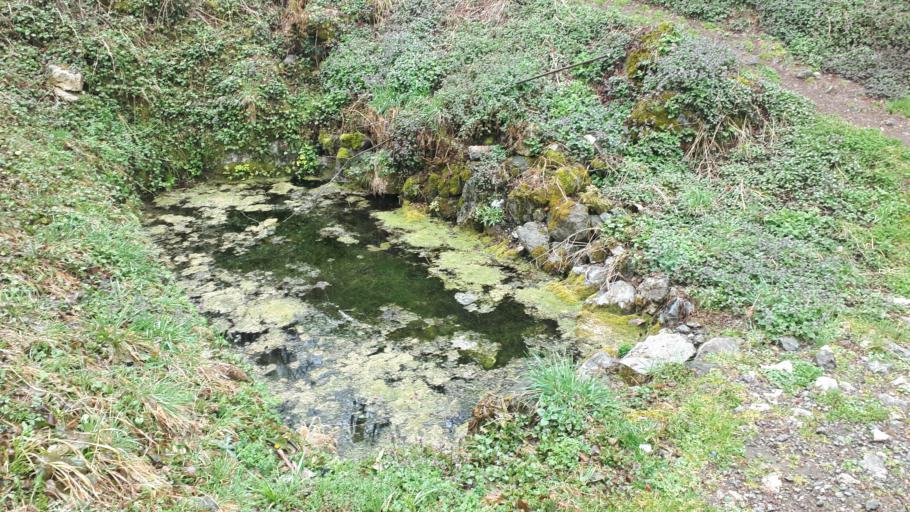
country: RS
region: Central Serbia
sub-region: Zlatiborski Okrug
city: Uzice
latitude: 43.8446
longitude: 19.7533
